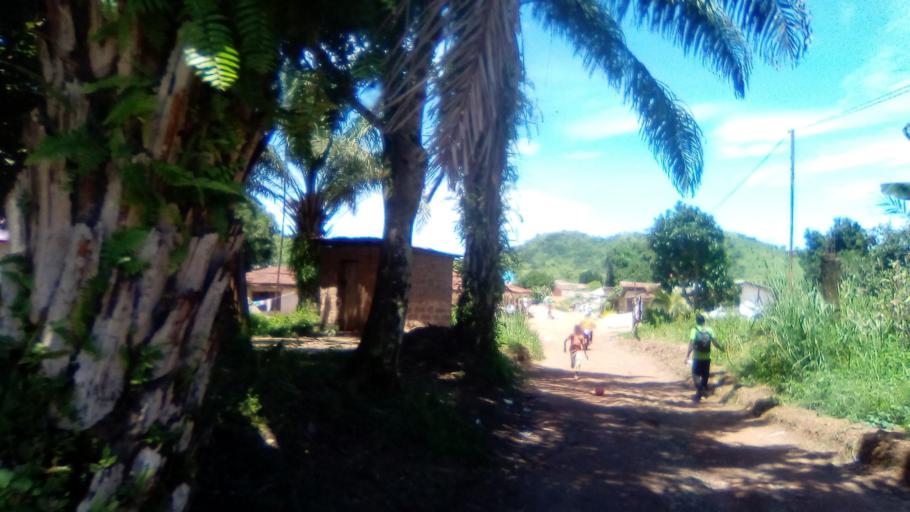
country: SL
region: Eastern Province
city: Simbakoro
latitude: 8.6220
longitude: -10.9950
